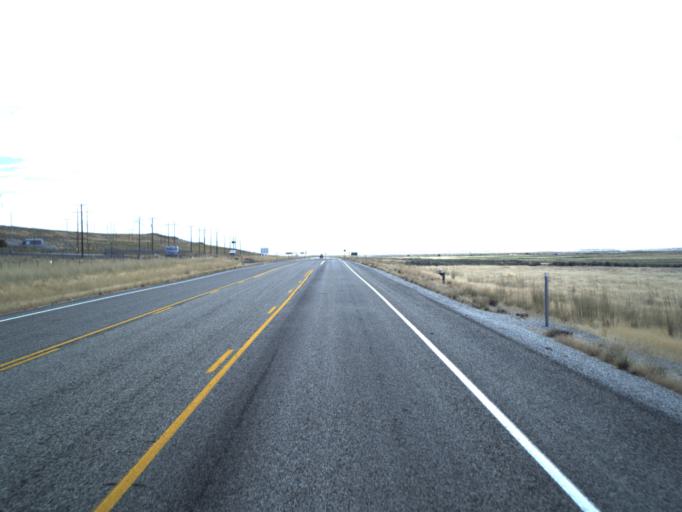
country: US
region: Utah
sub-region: Box Elder County
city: Tremonton
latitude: 41.6404
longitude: -112.4273
